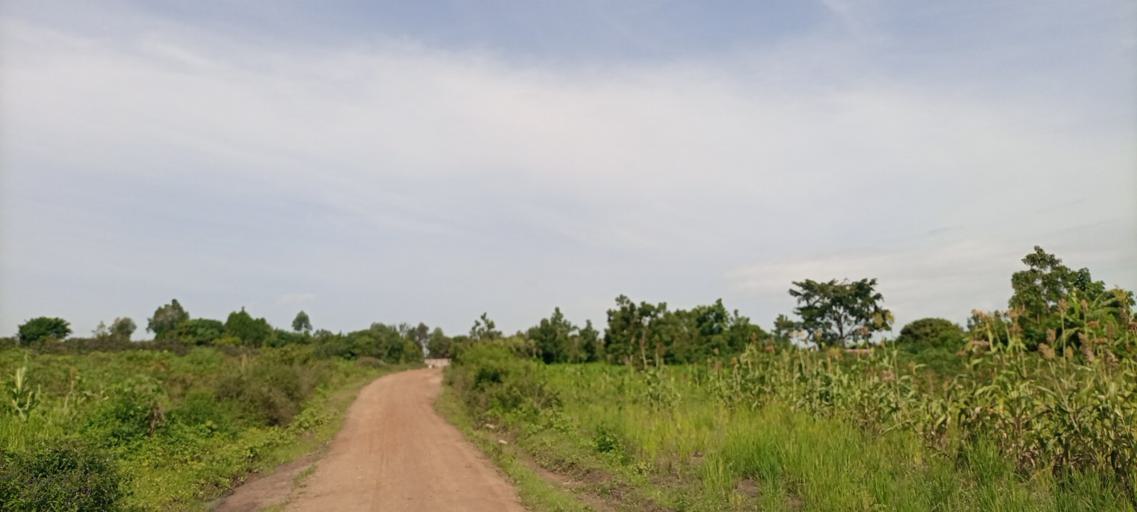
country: UG
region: Eastern Region
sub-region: Mbale District
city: Mbale
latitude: 1.1273
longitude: 34.0329
